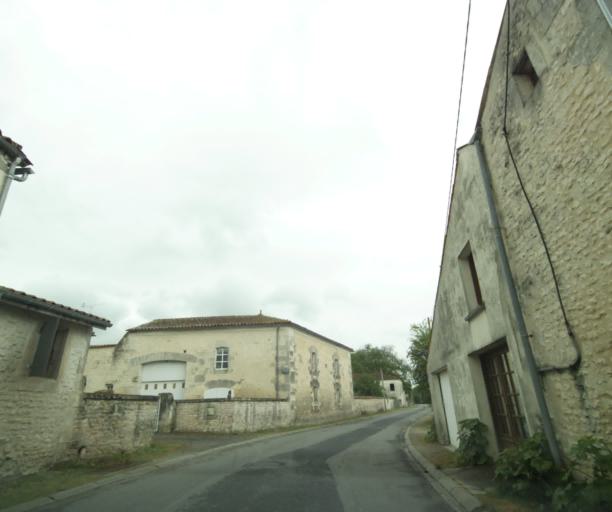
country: FR
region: Poitou-Charentes
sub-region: Departement de la Charente-Maritime
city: Chaniers
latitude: 45.6942
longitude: -0.5087
